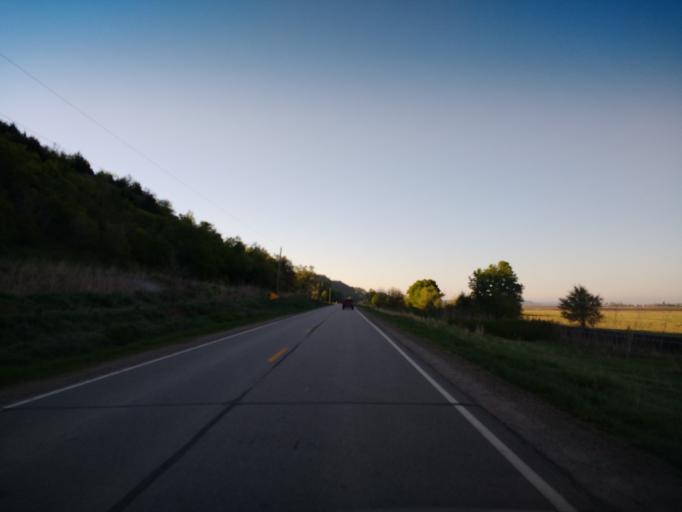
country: US
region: Iowa
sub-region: Harrison County
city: Missouri Valley
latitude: 41.4874
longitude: -95.8872
